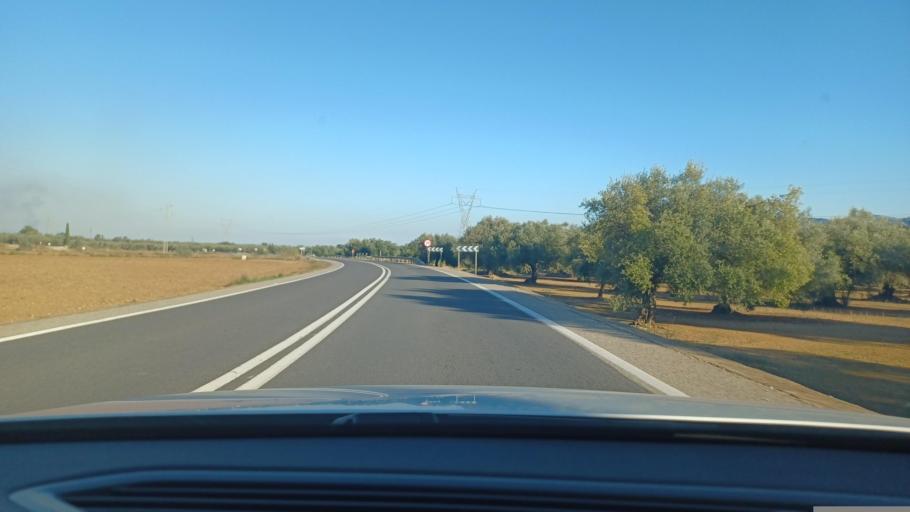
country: ES
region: Catalonia
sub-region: Provincia de Tarragona
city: Ulldecona
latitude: 40.6676
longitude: 0.4359
